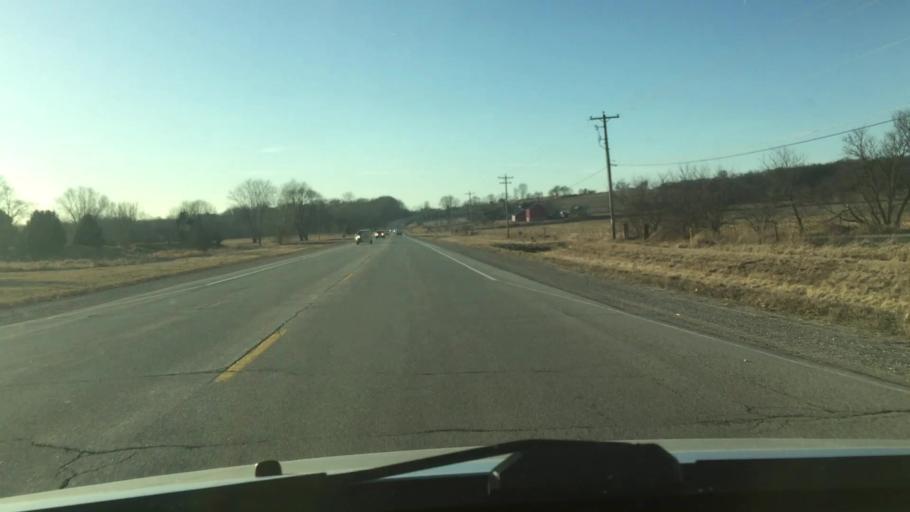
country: US
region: Wisconsin
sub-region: Waukesha County
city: Pewaukee
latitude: 43.1124
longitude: -88.2538
